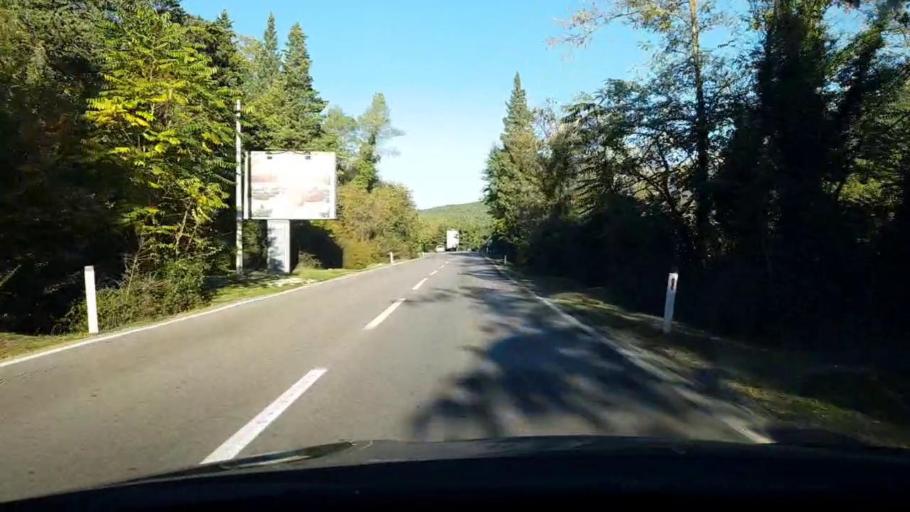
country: ME
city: Igalo
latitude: 42.4778
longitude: 18.4621
